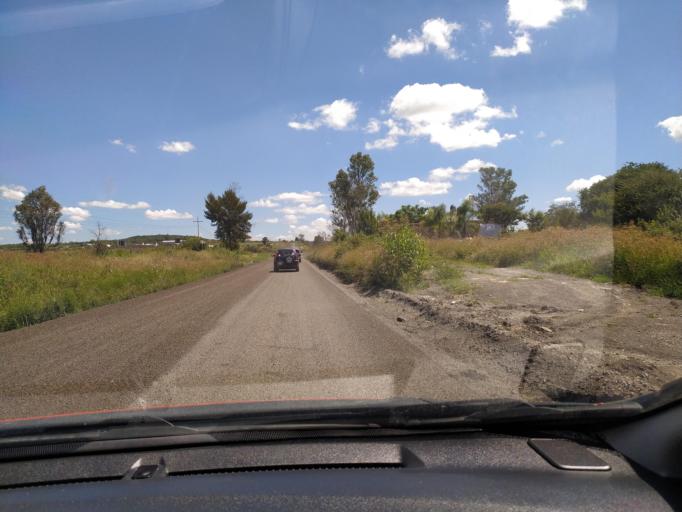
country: MX
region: Jalisco
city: San Julian
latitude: 21.0013
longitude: -102.0929
